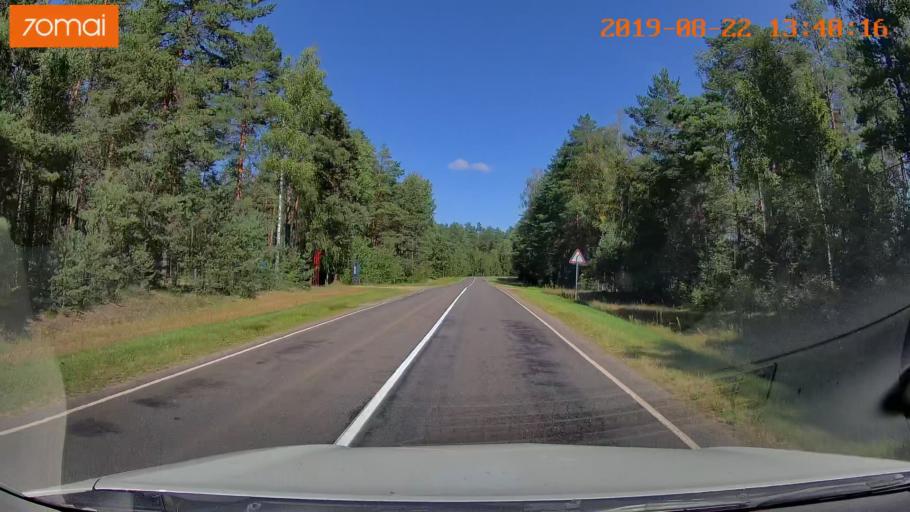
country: BY
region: Minsk
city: Staryya Darohi
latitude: 53.2356
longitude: 28.3643
